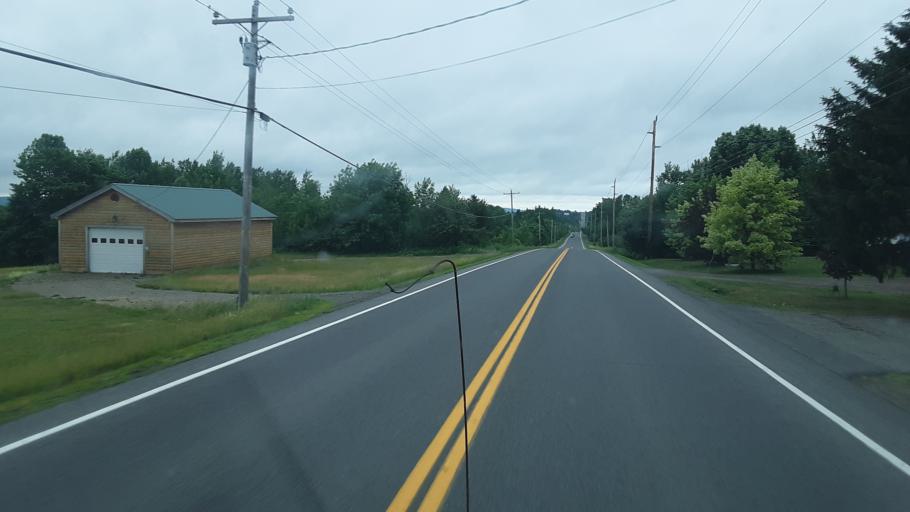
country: US
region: Maine
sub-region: Penobscot County
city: Patten
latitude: 45.9794
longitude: -68.4503
